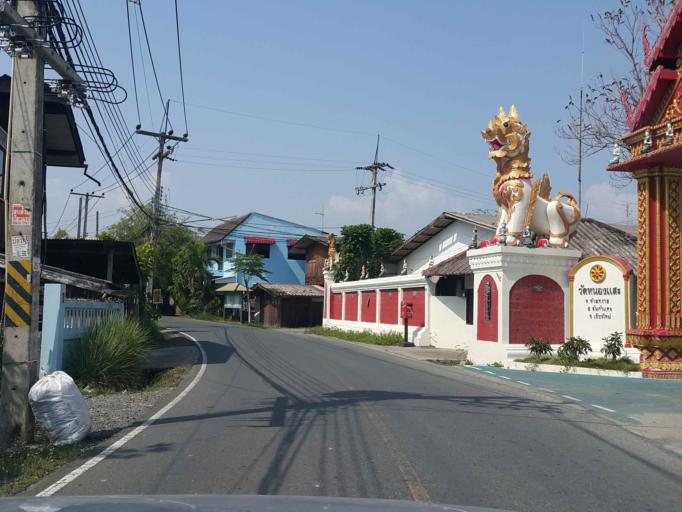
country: TH
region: Chiang Mai
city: San Kamphaeng
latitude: 18.7984
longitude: 99.1709
